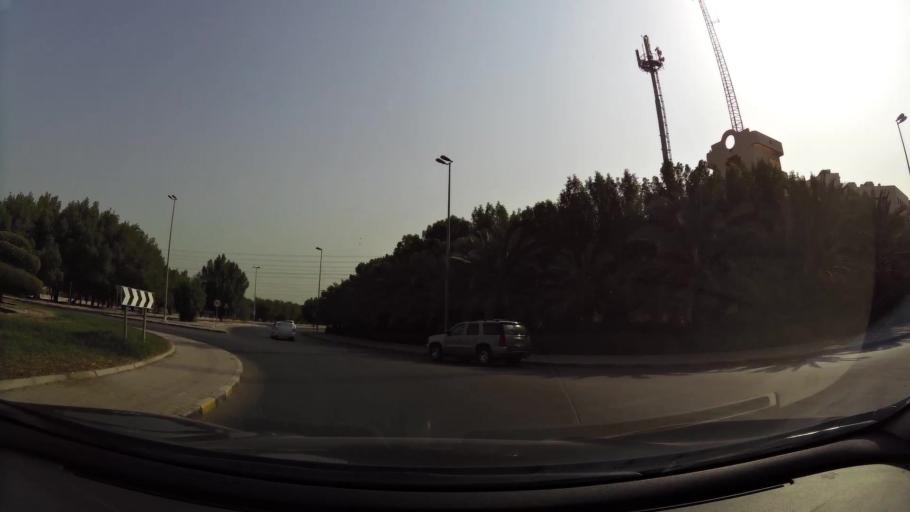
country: KW
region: Mubarak al Kabir
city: Sabah as Salim
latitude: 29.2680
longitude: 48.0563
